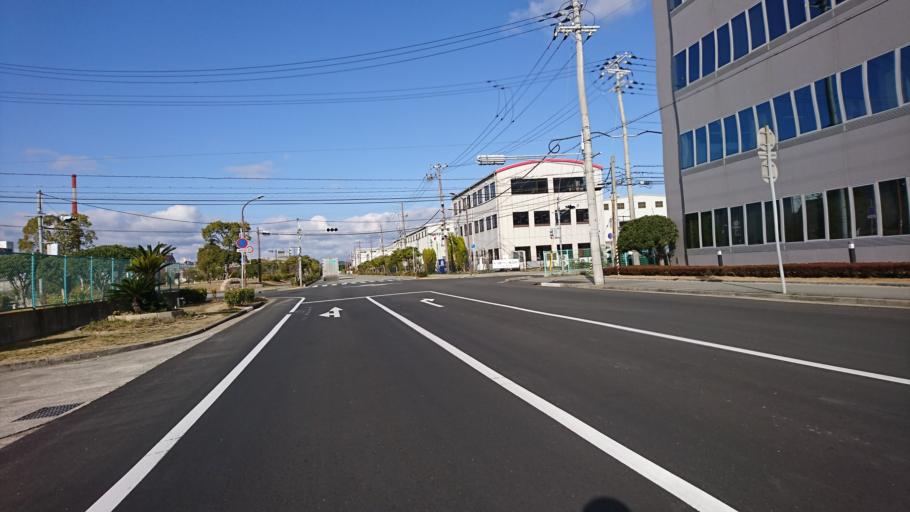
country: JP
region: Hyogo
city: Kakogawacho-honmachi
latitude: 34.7554
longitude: 134.7894
